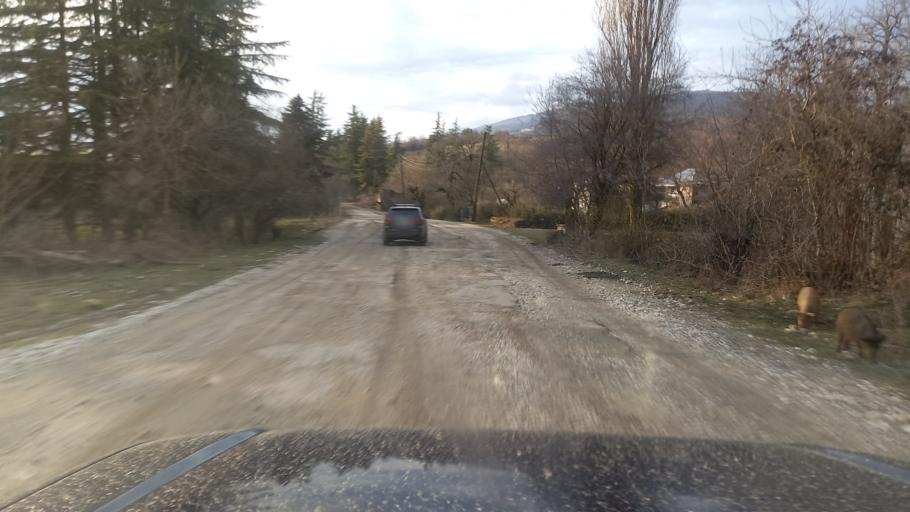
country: GE
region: Abkhazia
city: Dranda
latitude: 43.0211
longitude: 41.2803
